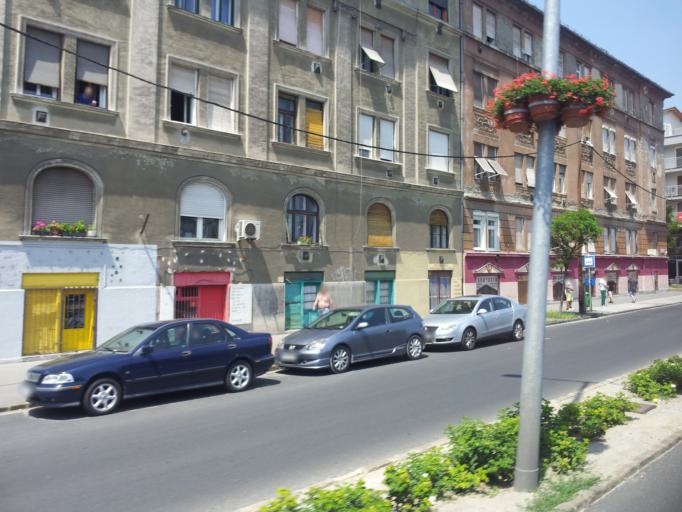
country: HU
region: Budapest
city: Budapest XIII. keruelet
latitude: 47.5310
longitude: 19.0856
